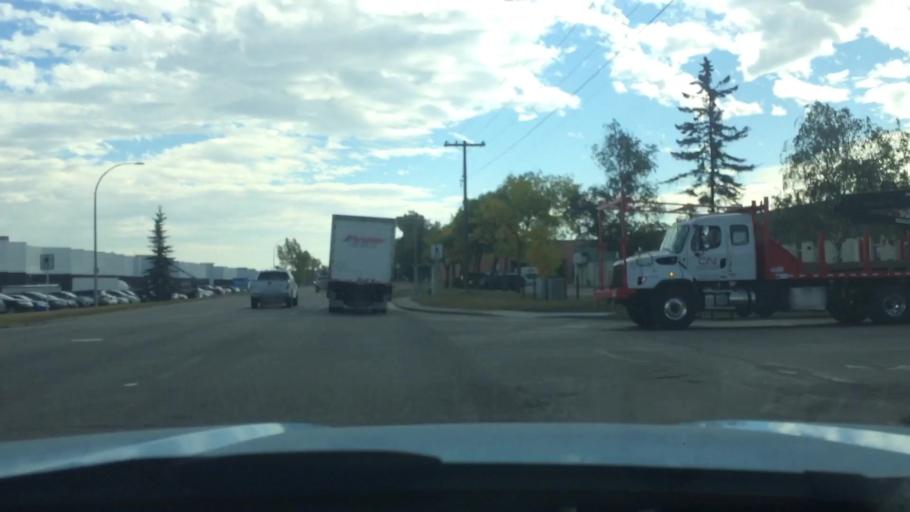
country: CA
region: Alberta
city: Calgary
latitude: 50.9990
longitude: -113.9768
